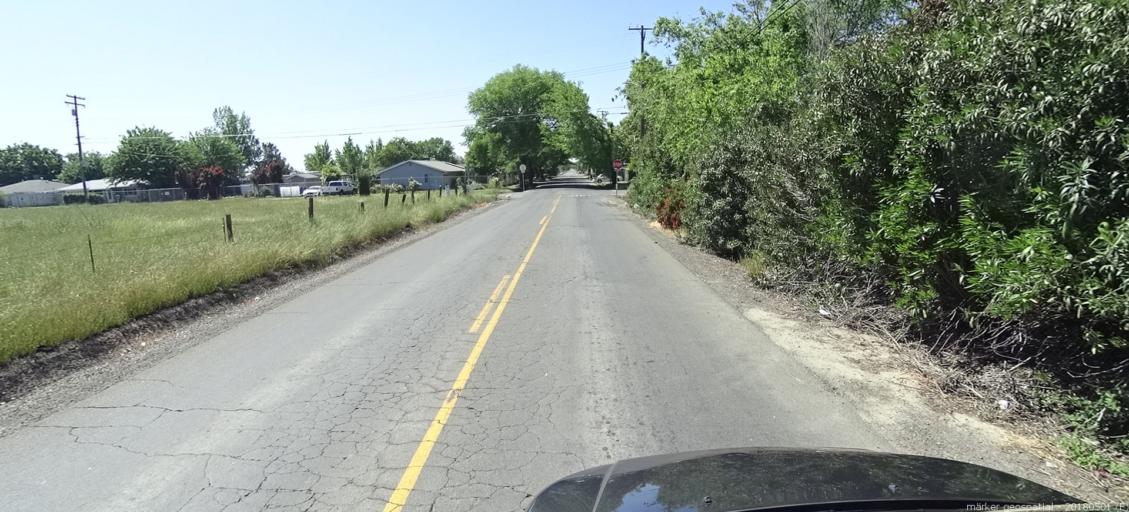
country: US
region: California
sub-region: Sacramento County
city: Rio Linda
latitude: 38.6625
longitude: -121.4384
